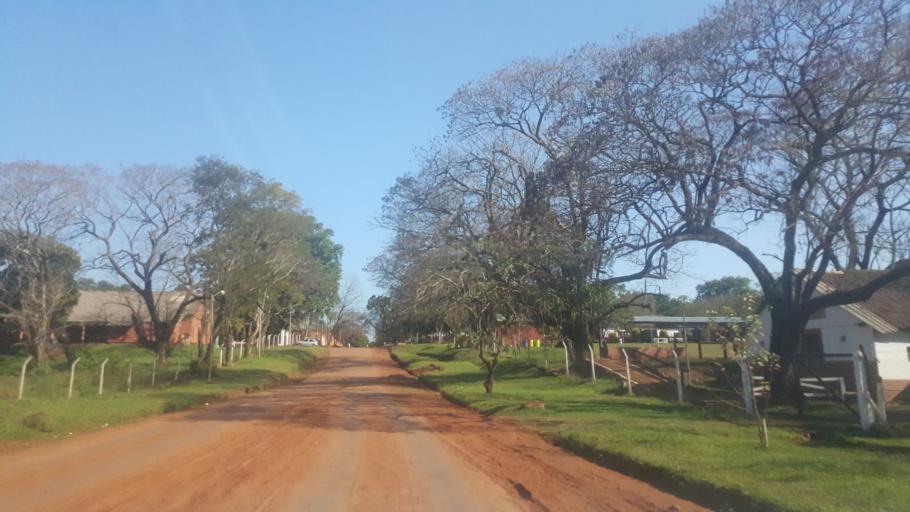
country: AR
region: Misiones
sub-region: Departamento de Capital
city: Posadas
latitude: -27.3623
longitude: -55.9197
